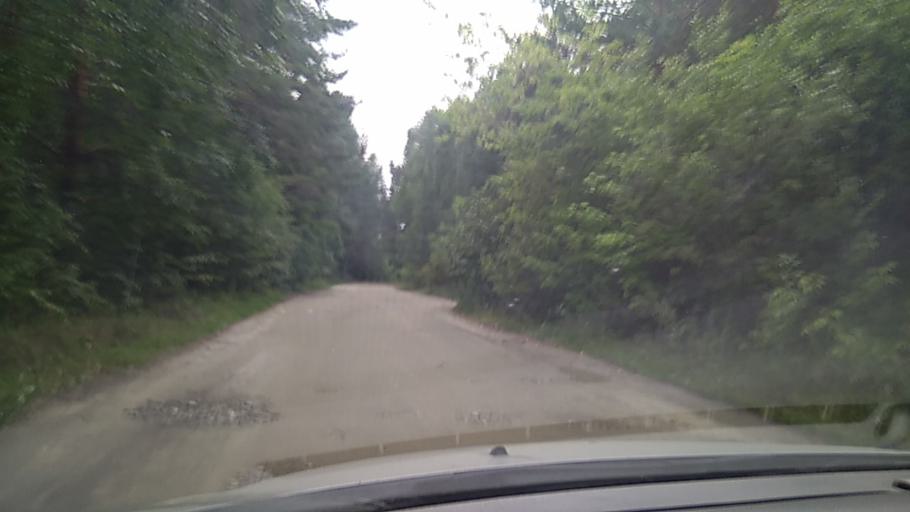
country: RU
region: Chelyabinsk
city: Kyshtym
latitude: 55.6790
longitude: 60.5814
